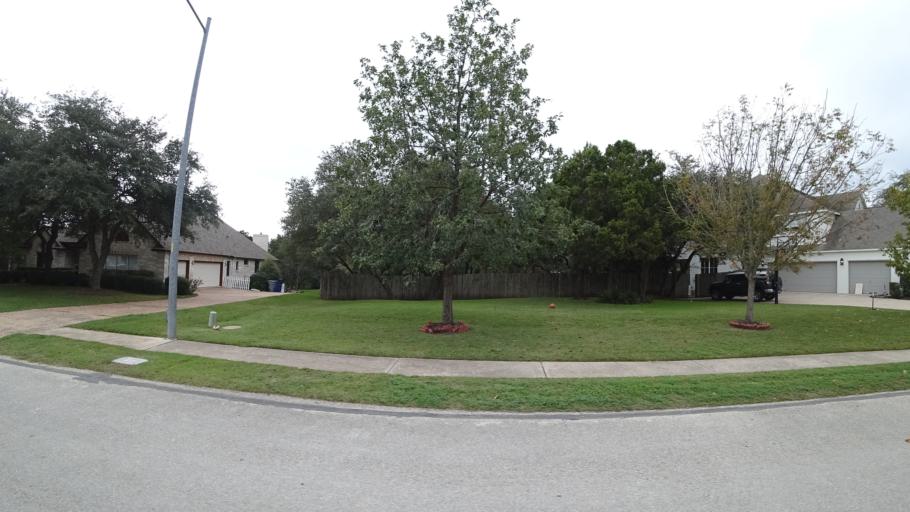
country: US
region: Texas
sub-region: Travis County
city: Barton Creek
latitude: 30.2564
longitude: -97.9074
